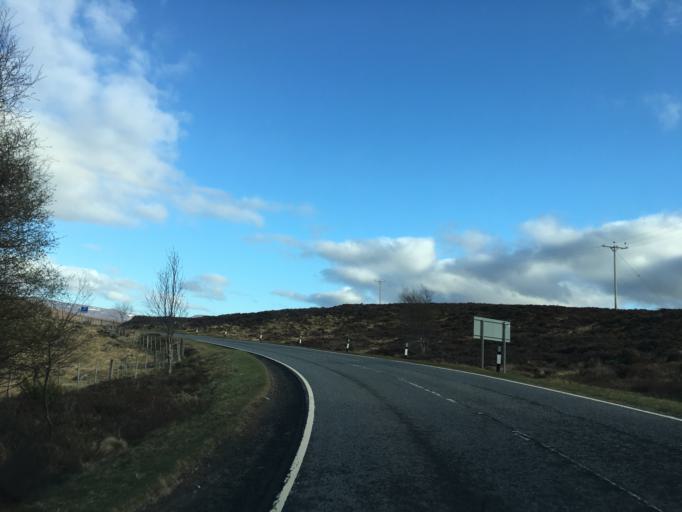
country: GB
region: Scotland
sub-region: Highland
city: Kingussie
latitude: 56.9980
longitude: -4.2503
